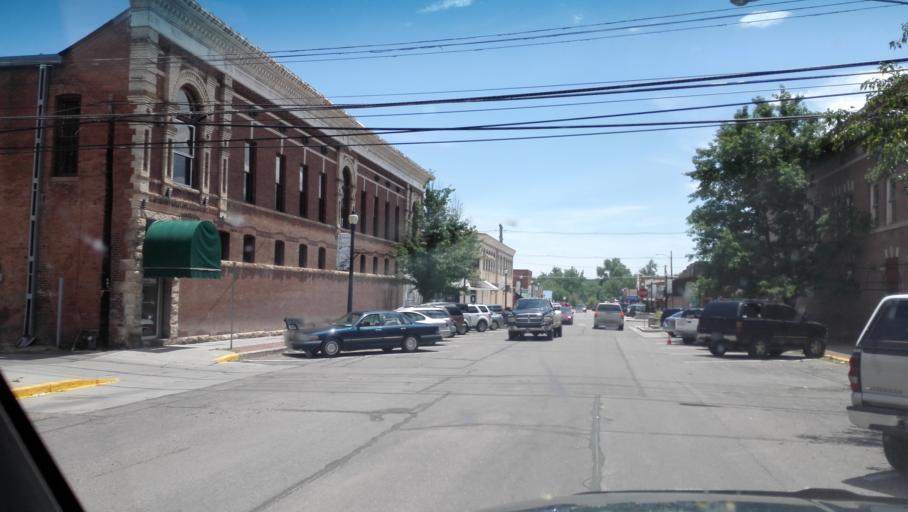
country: US
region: Colorado
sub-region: Fremont County
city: Canon City
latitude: 38.4411
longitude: -105.2412
